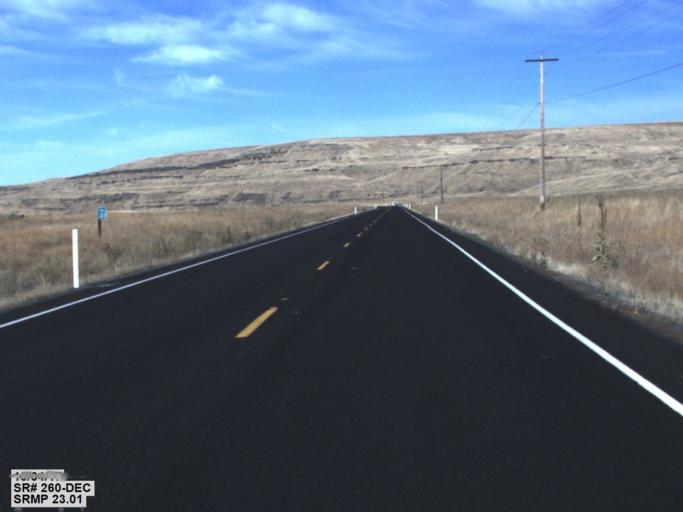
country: US
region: Washington
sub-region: Franklin County
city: Connell
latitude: 46.6486
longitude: -118.5925
